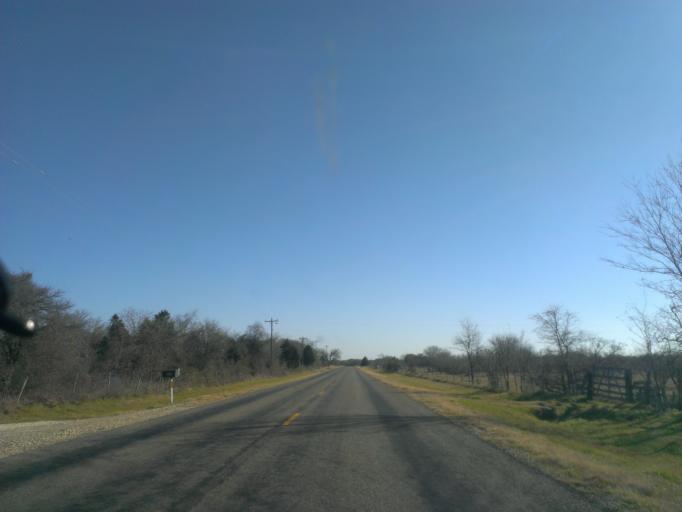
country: US
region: Texas
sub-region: Bastrop County
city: Elgin
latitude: 30.4512
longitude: -97.2661
